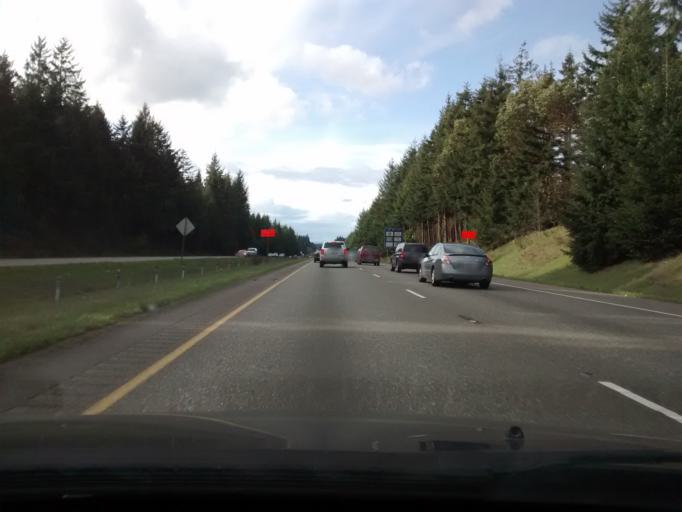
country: US
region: Washington
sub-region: Pierce County
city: Gig Harbor
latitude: 47.3102
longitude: -122.5807
